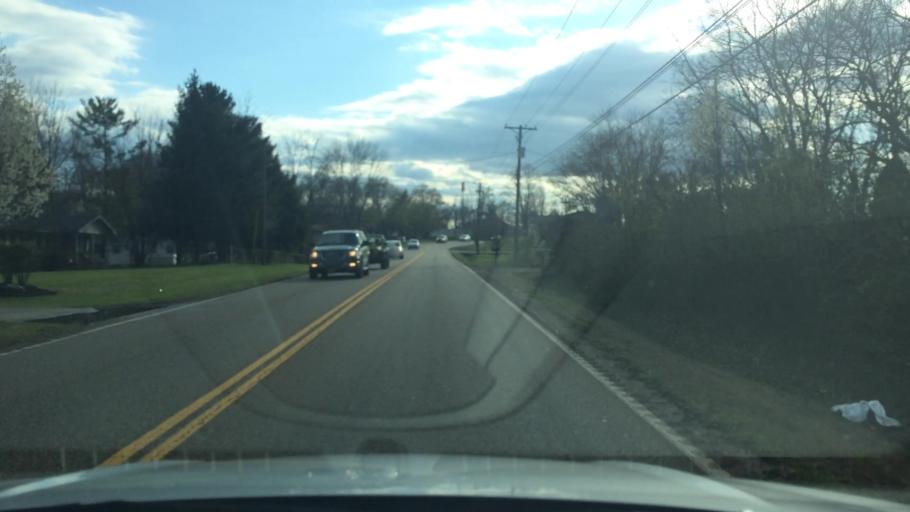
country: US
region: Tennessee
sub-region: Sevier County
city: Seymour
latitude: 35.8731
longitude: -83.7526
